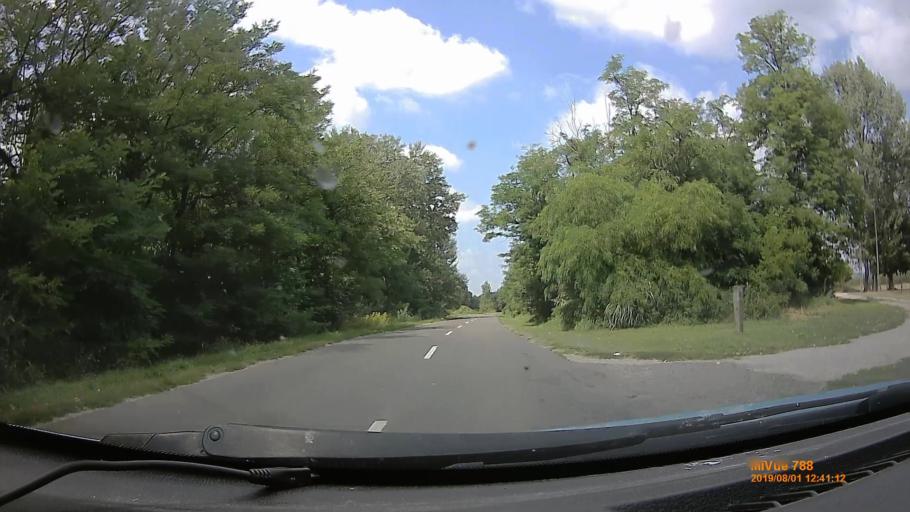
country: HU
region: Baranya
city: Harkany
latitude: 45.8355
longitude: 18.1780
